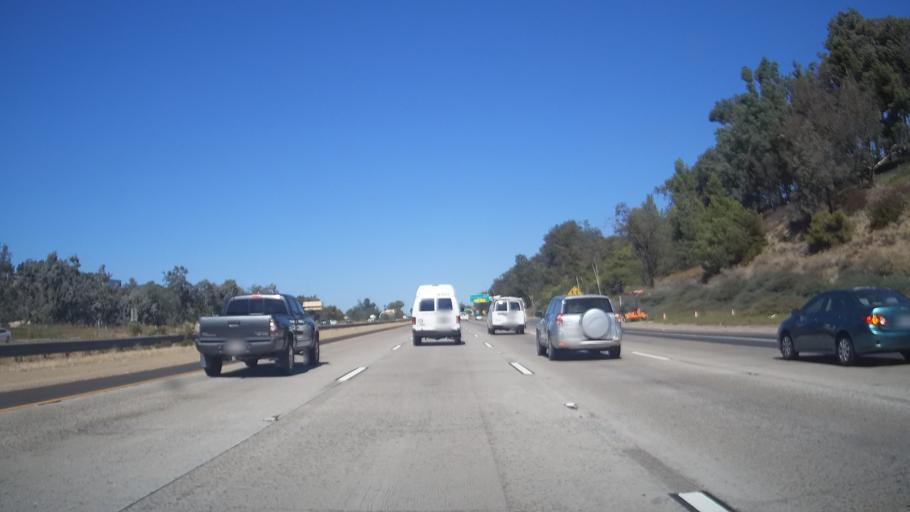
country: US
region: California
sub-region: San Diego County
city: La Mesa
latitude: 32.8239
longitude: -117.1165
